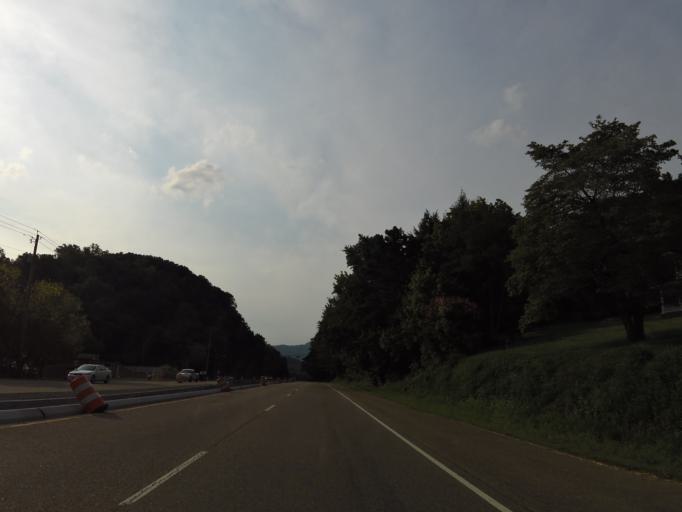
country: US
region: Tennessee
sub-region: Roane County
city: Oliver Springs
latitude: 36.0386
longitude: -84.3343
